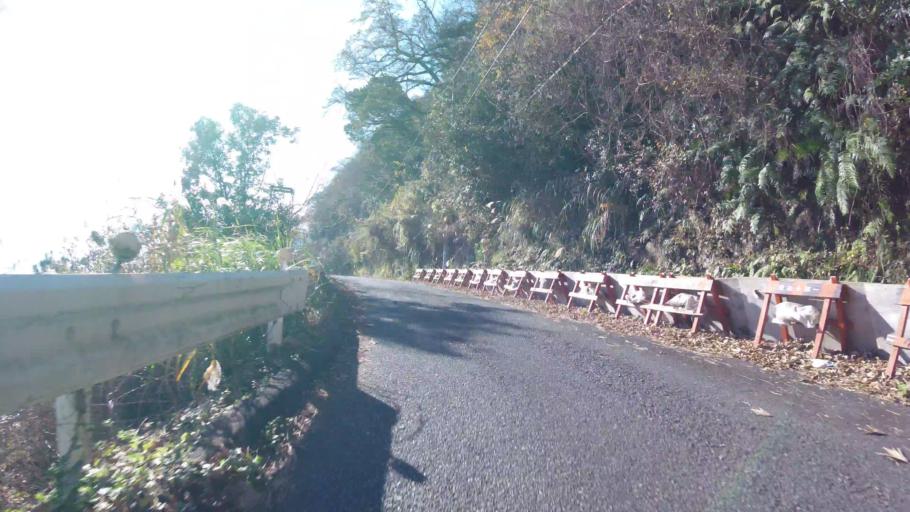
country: JP
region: Shizuoka
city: Atami
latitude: 35.0719
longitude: 139.0774
